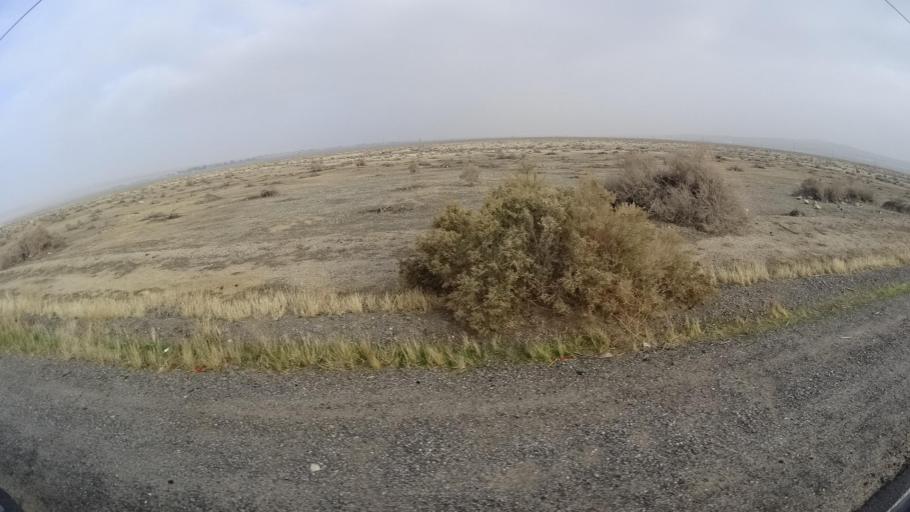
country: US
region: California
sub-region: Kern County
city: Ford City
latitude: 35.2006
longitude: -119.4456
